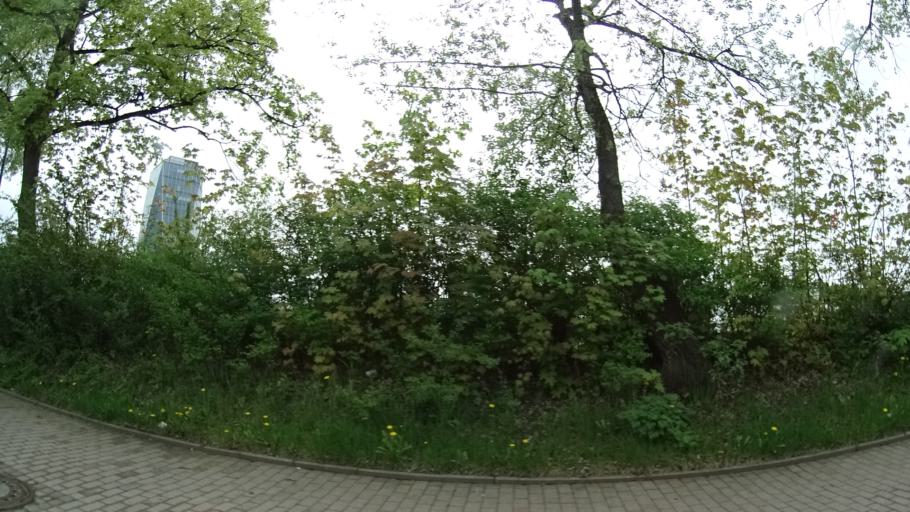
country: DE
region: Baden-Wuerttemberg
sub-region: Freiburg Region
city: Dauchingen
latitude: 48.0607
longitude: 8.5362
